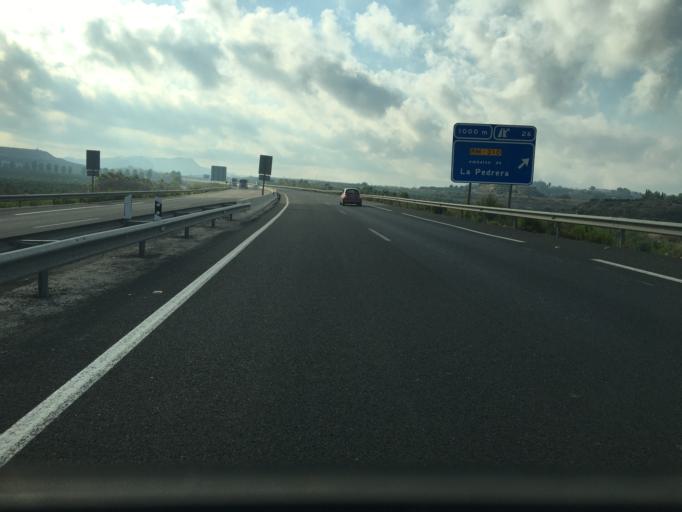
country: ES
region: Murcia
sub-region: Murcia
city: Beniel
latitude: 37.9957
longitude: -1.0023
